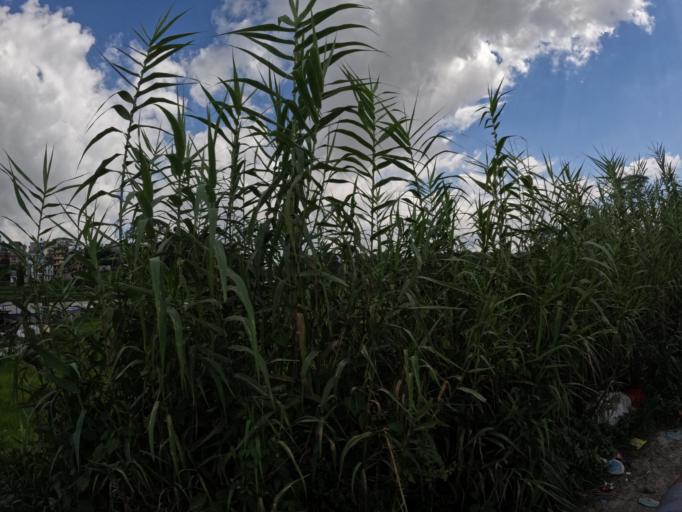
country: NP
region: Central Region
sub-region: Bagmati Zone
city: Kathmandu
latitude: 27.7676
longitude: 85.3272
